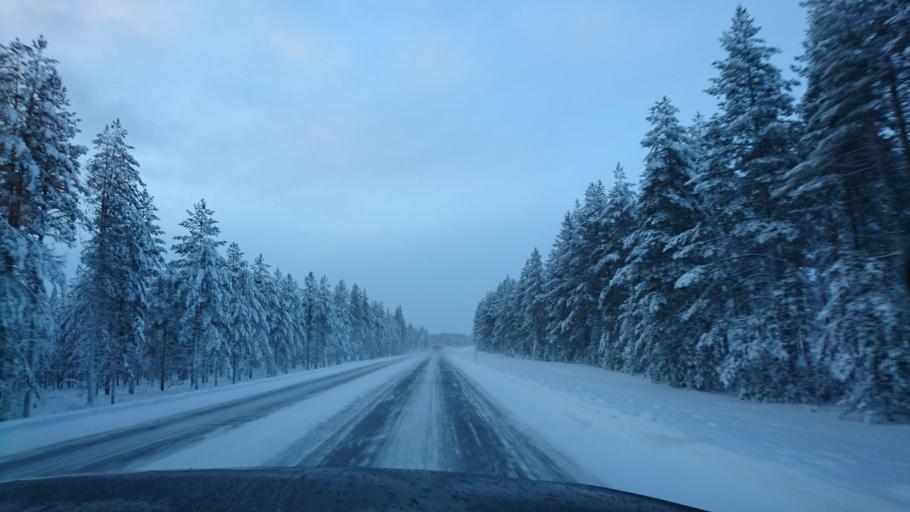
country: FI
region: Kainuu
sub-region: Kehys-Kainuu
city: Puolanka
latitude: 65.4367
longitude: 27.5940
